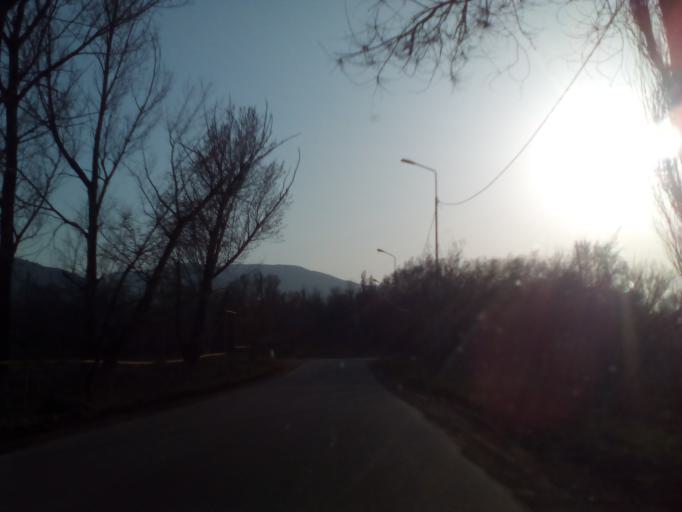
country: KZ
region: Almaty Oblysy
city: Burunday
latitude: 43.1607
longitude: 76.4548
